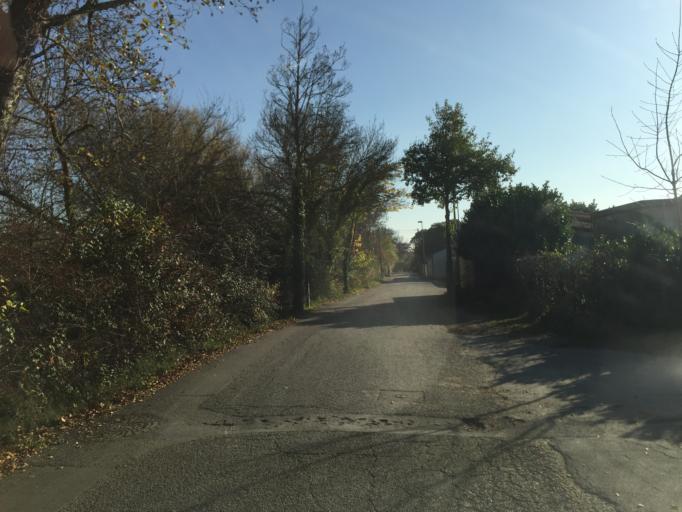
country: FR
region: Provence-Alpes-Cote d'Azur
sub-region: Departement du Vaucluse
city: Entraigues-sur-la-Sorgue
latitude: 44.0069
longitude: 4.9289
